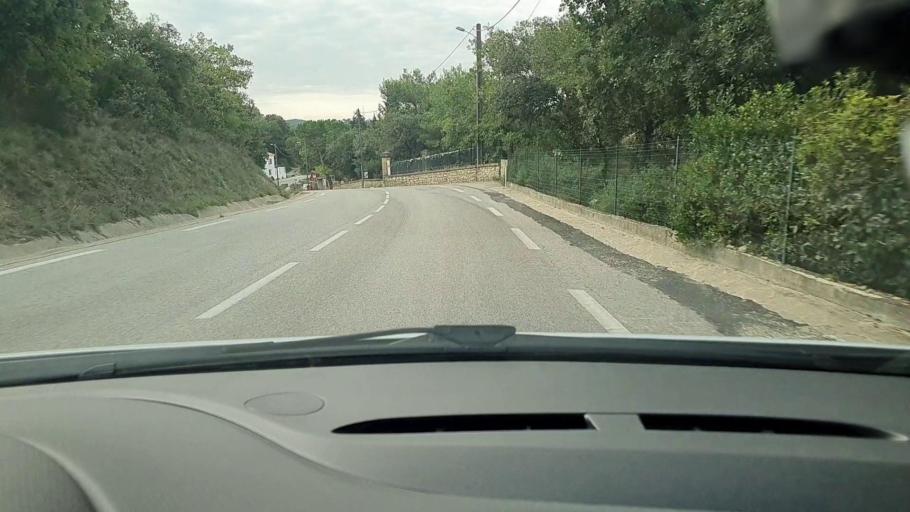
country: FR
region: Languedoc-Roussillon
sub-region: Departement du Gard
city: Mons
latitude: 44.1127
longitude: 4.2245
